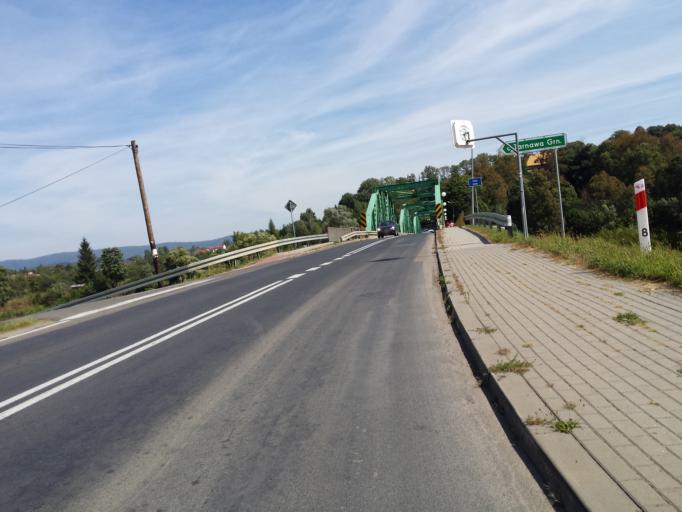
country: PL
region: Subcarpathian Voivodeship
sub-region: Powiat leski
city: Lesko
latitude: 49.4681
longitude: 22.3203
